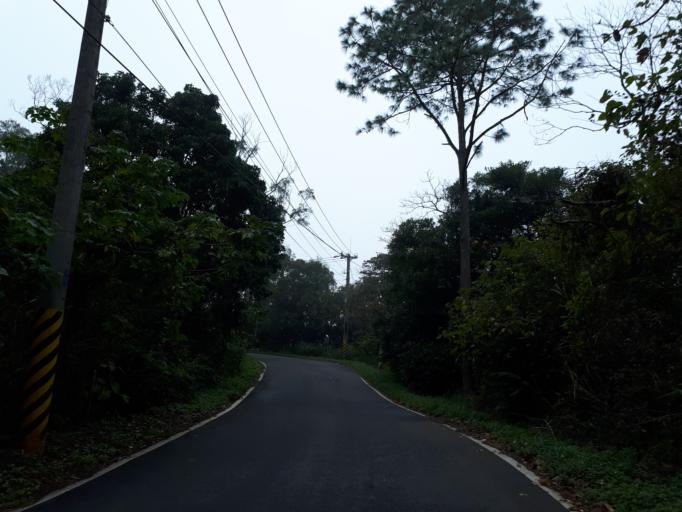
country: TW
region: Taiwan
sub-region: Hsinchu
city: Zhubei
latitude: 24.7335
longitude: 121.0746
